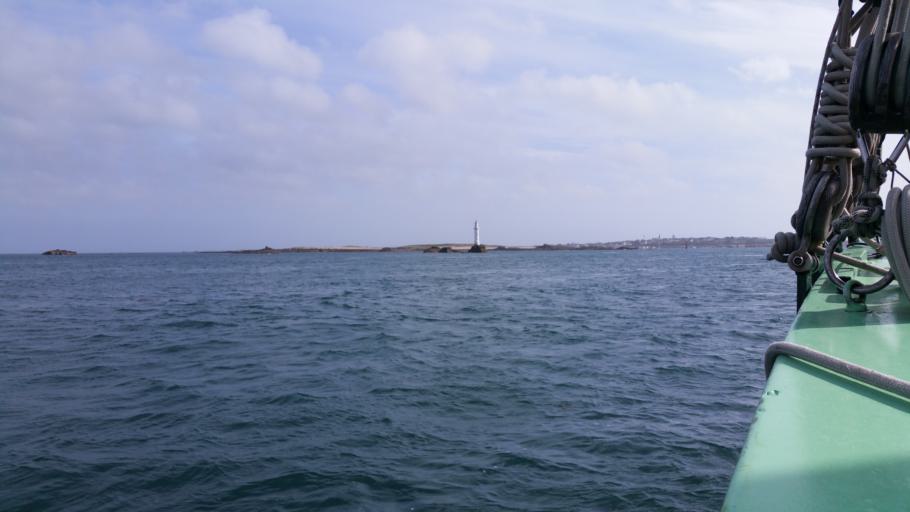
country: FR
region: Brittany
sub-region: Departement du Finistere
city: Le Conquet
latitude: 48.4156
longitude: -4.9464
